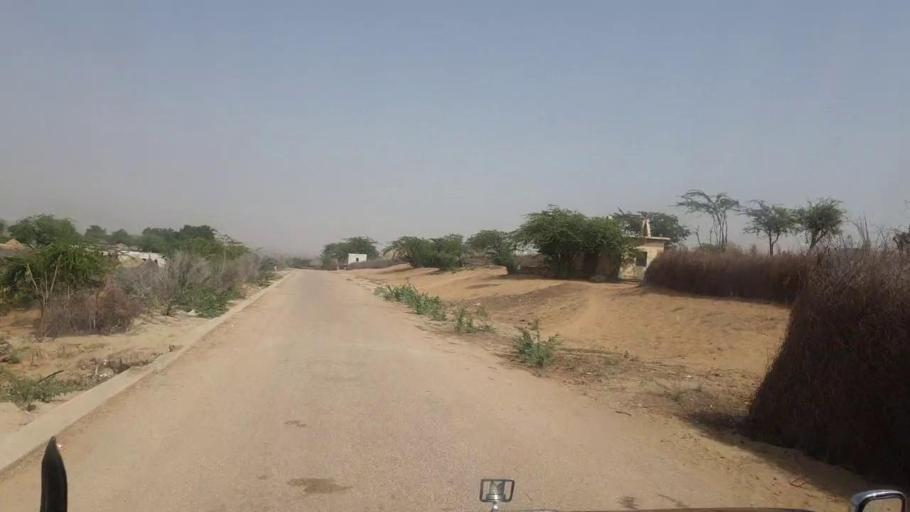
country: PK
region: Sindh
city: Umarkot
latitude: 25.2303
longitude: 70.2454
